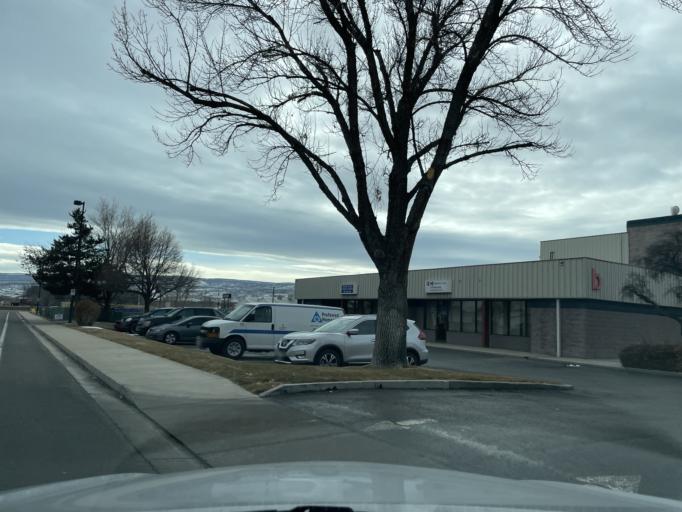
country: US
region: Colorado
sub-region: Mesa County
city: Grand Junction
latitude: 39.0824
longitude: -108.5802
